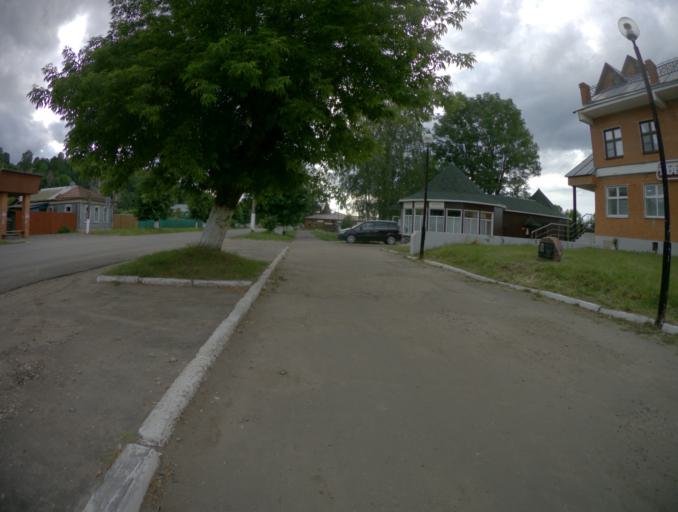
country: RU
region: Vladimir
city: Gorokhovets
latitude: 56.2021
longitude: 42.6906
